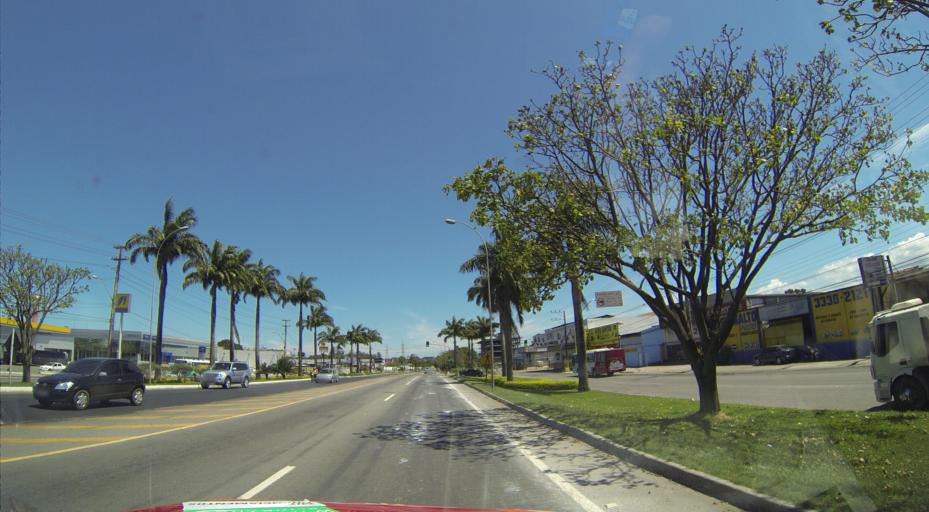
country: BR
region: Espirito Santo
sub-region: Serra
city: Serra
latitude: -20.2229
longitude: -40.2704
